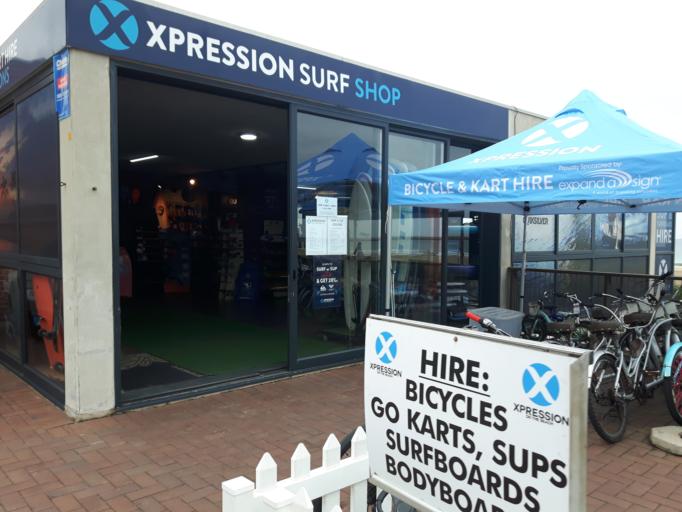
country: ZA
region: KwaZulu-Natal
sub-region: eThekwini Metropolitan Municipality
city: Durban
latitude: -29.8646
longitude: 31.0438
